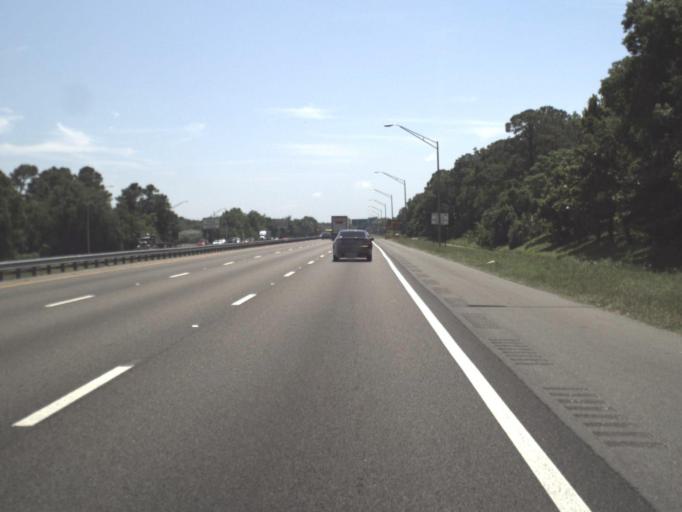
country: US
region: Florida
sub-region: Clay County
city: Bellair-Meadowbrook Terrace
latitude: 30.2362
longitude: -81.7631
